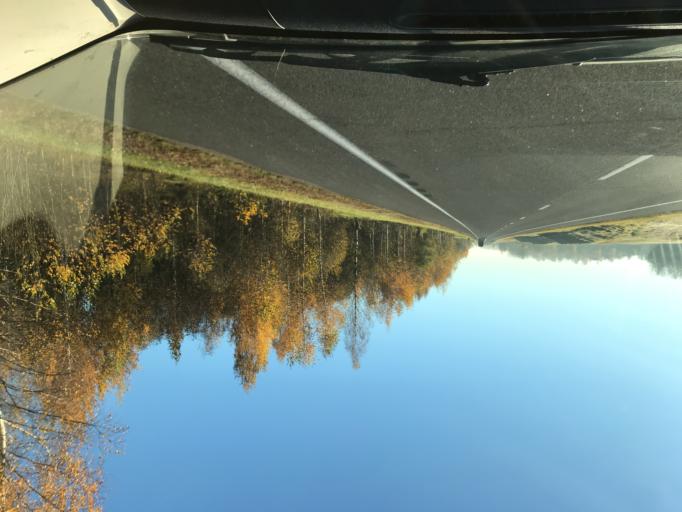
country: BY
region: Vitebsk
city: Vitebsk
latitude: 55.0079
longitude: 30.3330
